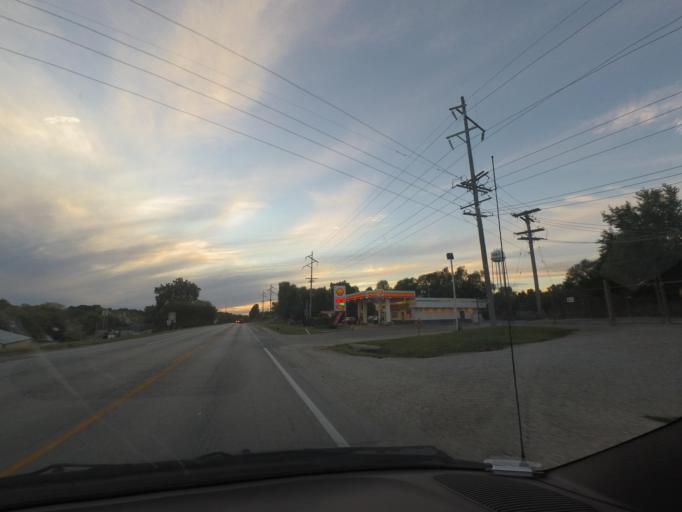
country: US
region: Illinois
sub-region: Pike County
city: Barry
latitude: 39.7006
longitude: -91.0415
